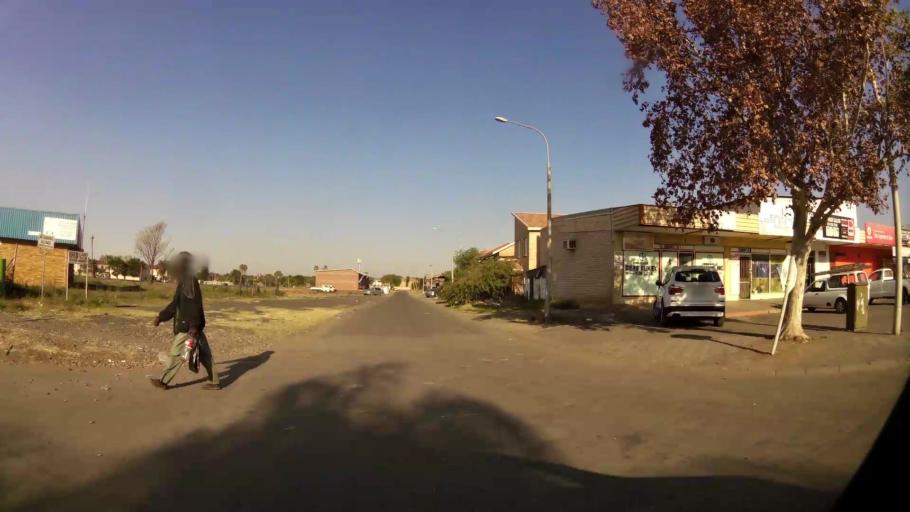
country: ZA
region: North-West
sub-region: Bojanala Platinum District Municipality
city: Rustenburg
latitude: -25.6485
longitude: 27.2398
